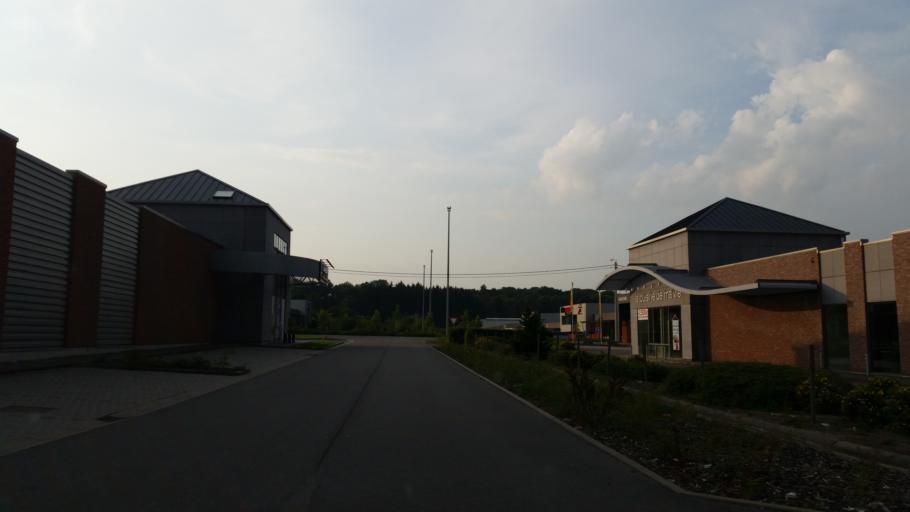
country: BE
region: Wallonia
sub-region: Province du Luxembourg
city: Marche-en-Famenne
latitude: 50.2216
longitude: 5.3314
